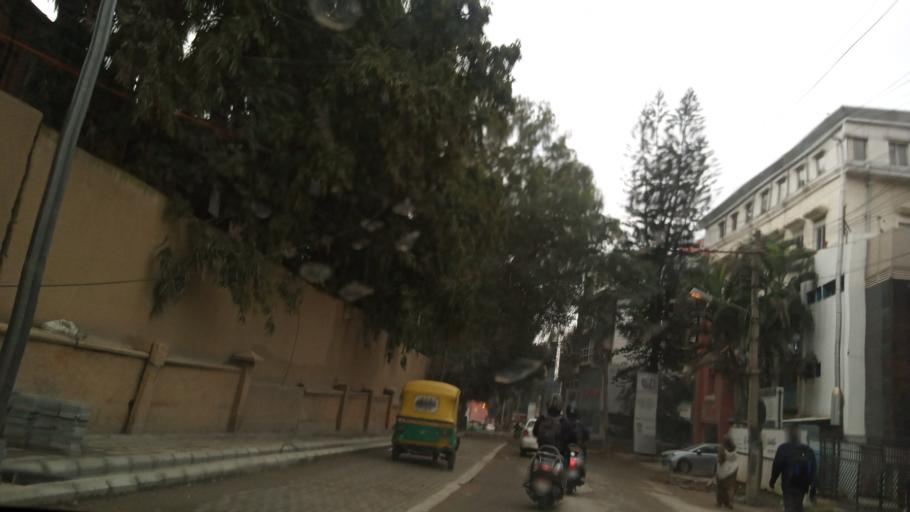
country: IN
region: Karnataka
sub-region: Bangalore Urban
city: Bangalore
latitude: 12.9745
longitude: 77.5996
